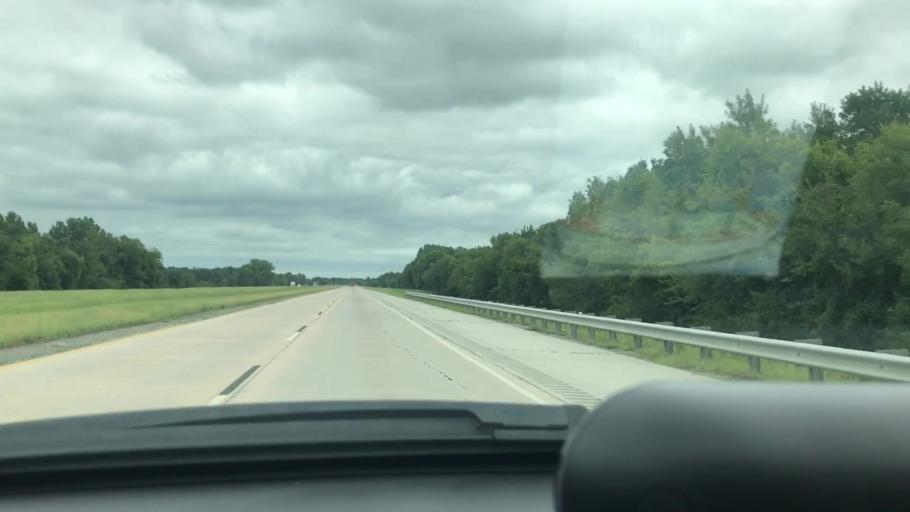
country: US
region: Oklahoma
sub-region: Wagoner County
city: Wagoner
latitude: 35.8944
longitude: -95.4026
